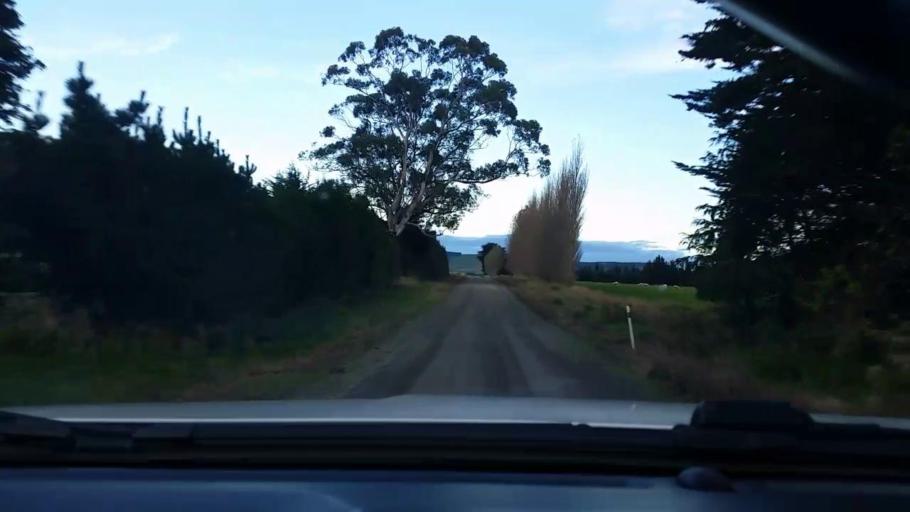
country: NZ
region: Southland
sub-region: Southland District
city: Winton
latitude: -46.1043
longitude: 168.4585
